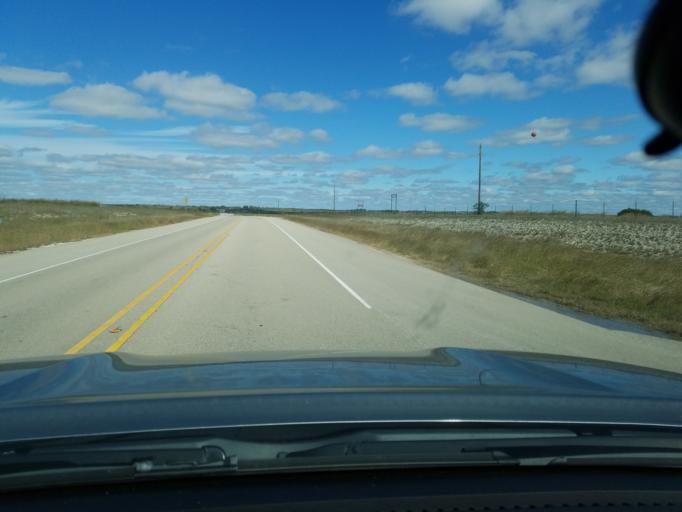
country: US
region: Texas
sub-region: Hamilton County
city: Hamilton
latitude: 31.6298
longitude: -98.1531
